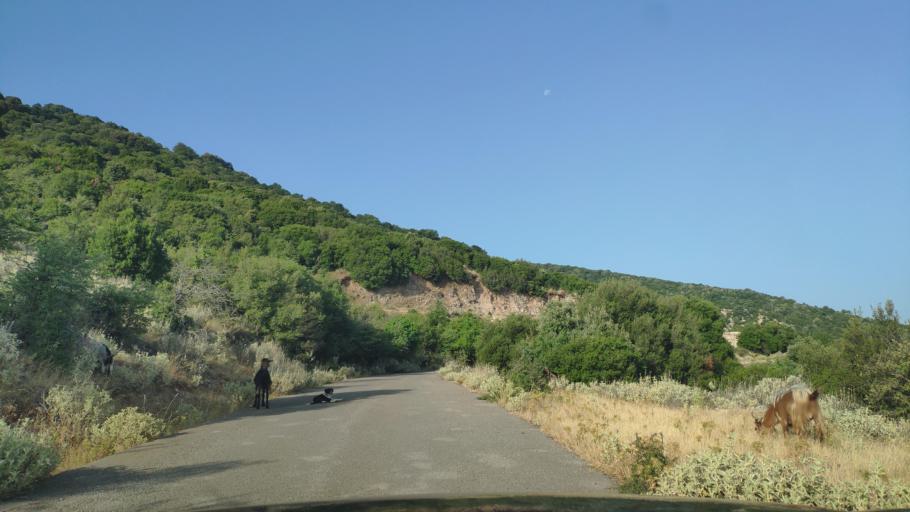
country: GR
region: West Greece
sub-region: Nomos Aitolias kai Akarnanias
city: Monastirakion
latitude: 38.8423
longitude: 20.9734
